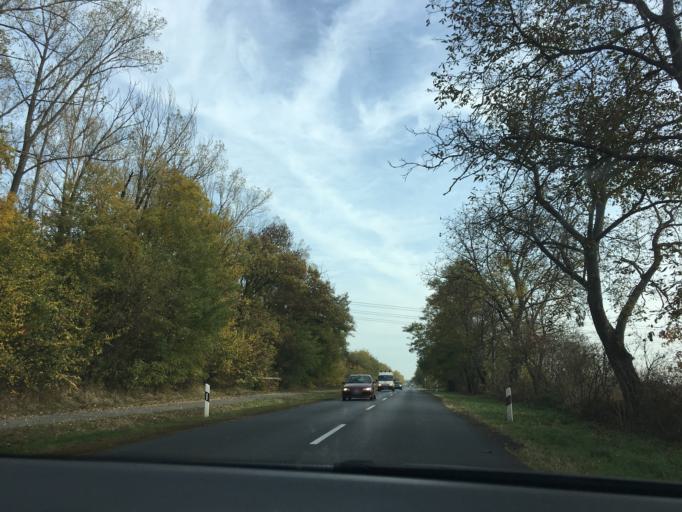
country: HU
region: Szabolcs-Szatmar-Bereg
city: Nagykallo
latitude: 47.8645
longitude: 21.8846
